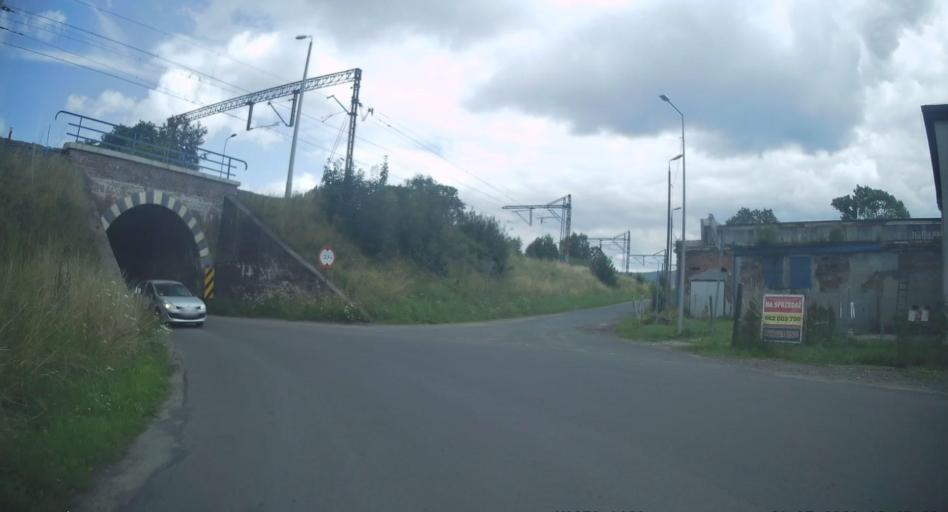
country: PL
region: Lower Silesian Voivodeship
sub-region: Powiat kamiennogorski
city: Marciszow
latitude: 50.8534
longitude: 16.0020
